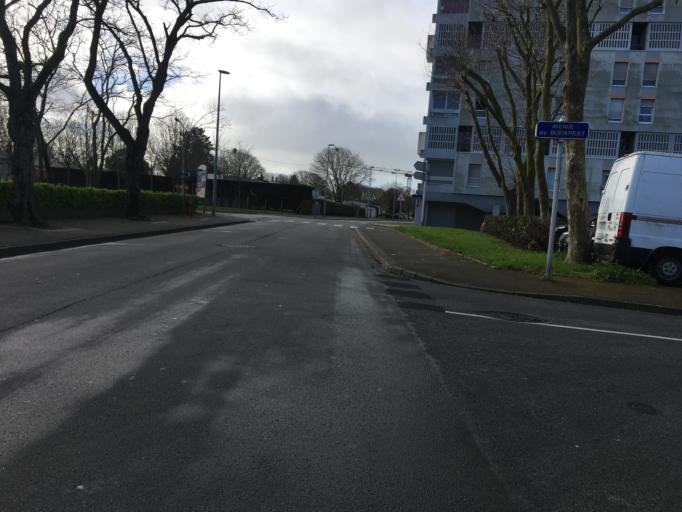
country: FR
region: Poitou-Charentes
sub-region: Departement de la Charente-Maritime
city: La Rochelle
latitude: 46.1687
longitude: -1.1870
